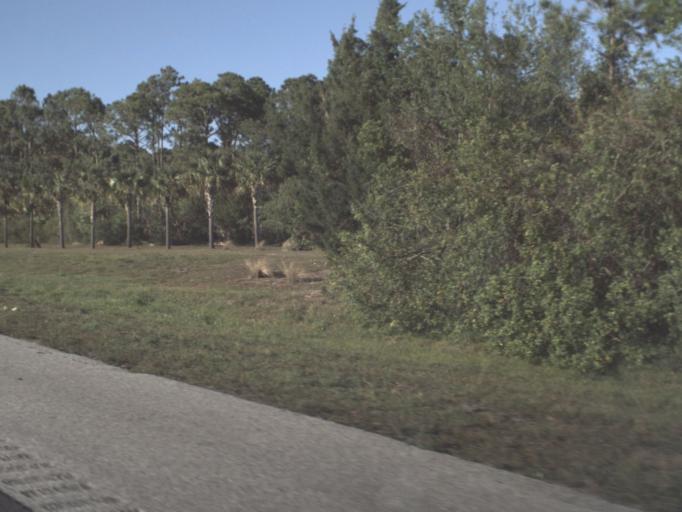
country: US
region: Florida
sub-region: Flagler County
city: Flagler Beach
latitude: 29.4077
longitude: -81.1567
